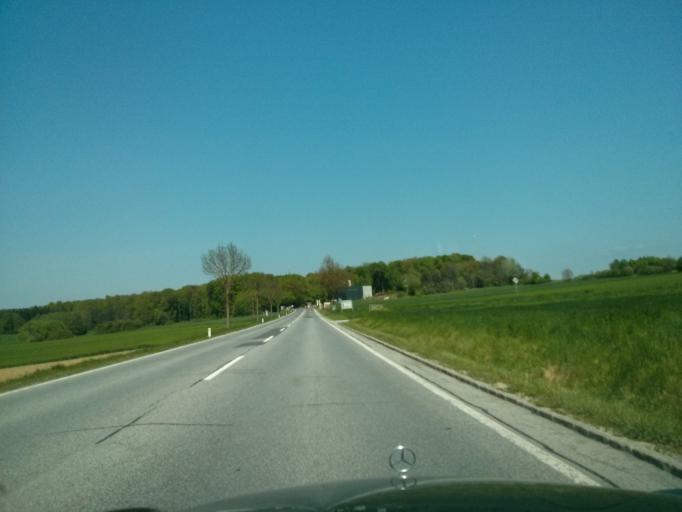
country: AT
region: Burgenland
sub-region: Politischer Bezirk Oberwart
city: Bad Tatzmannsdorf
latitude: 47.3226
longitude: 16.2162
